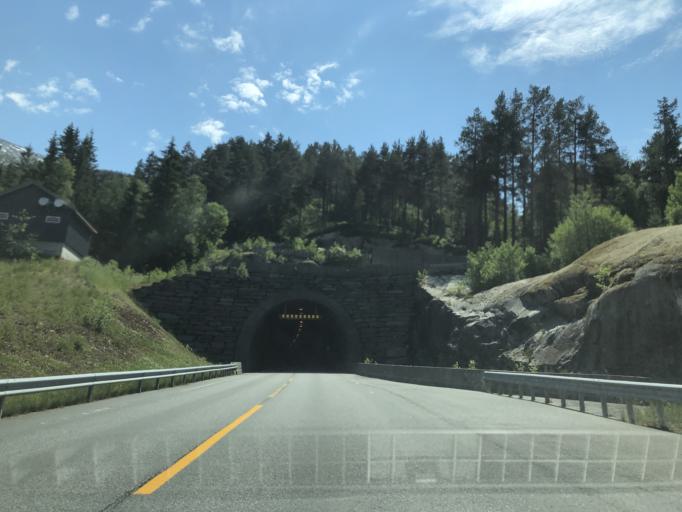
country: NO
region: Hordaland
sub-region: Jondal
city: Jondal
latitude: 60.2346
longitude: 6.2070
